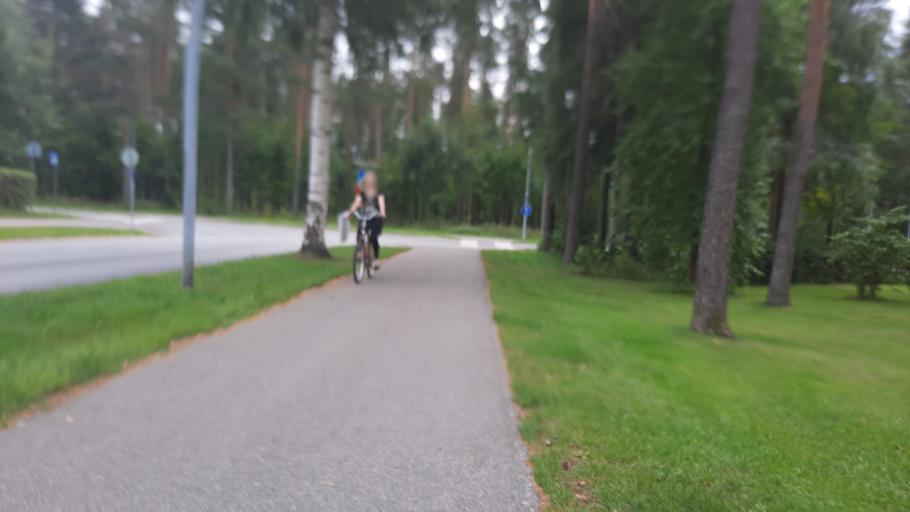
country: FI
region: North Karelia
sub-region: Joensuu
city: Joensuu
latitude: 62.6108
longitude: 29.8135
